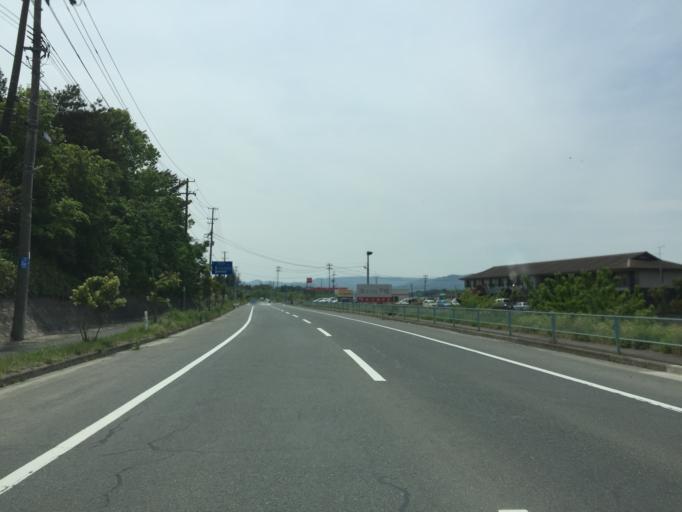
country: JP
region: Miyagi
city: Marumori
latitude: 37.8277
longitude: 140.9521
